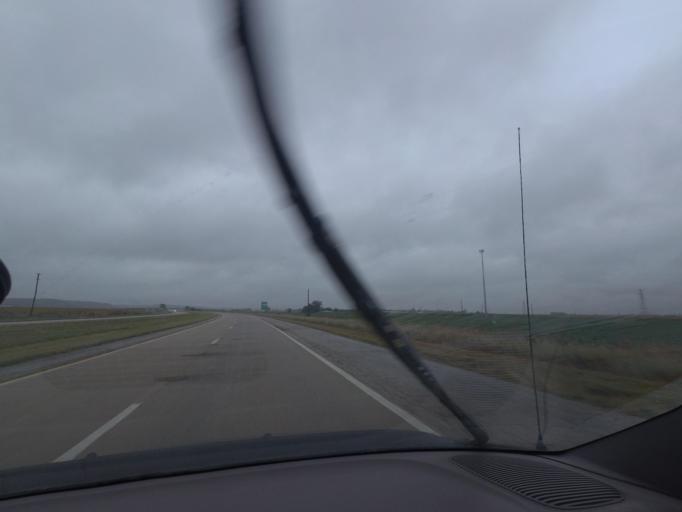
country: US
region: Illinois
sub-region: Adams County
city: Payson
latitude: 39.7226
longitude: -91.2244
